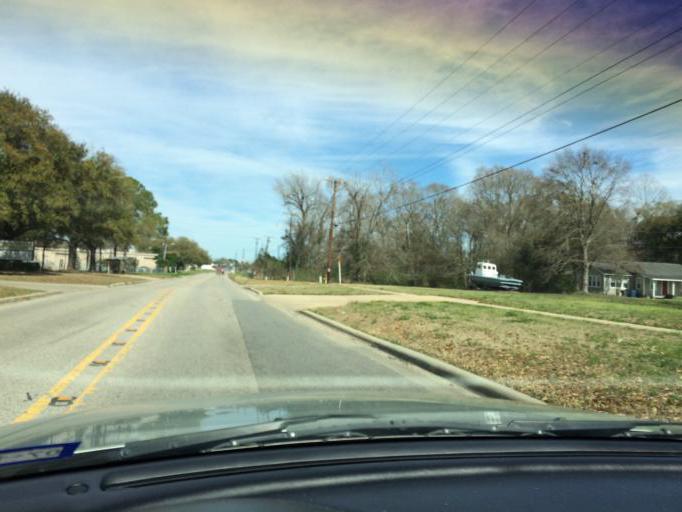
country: US
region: Louisiana
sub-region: Lafayette Parish
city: Lafayette
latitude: 30.2189
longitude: -92.0569
